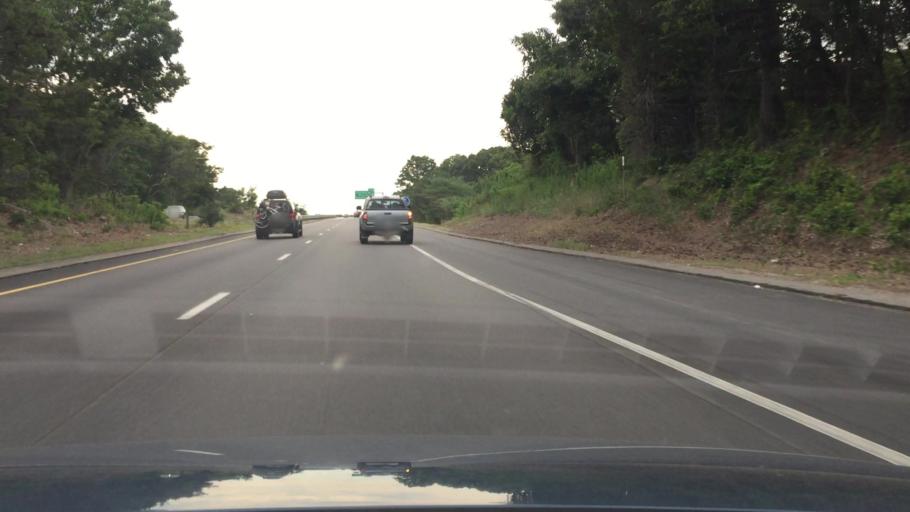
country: US
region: Massachusetts
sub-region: Plymouth County
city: Plymouth
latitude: 41.9342
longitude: -70.6498
